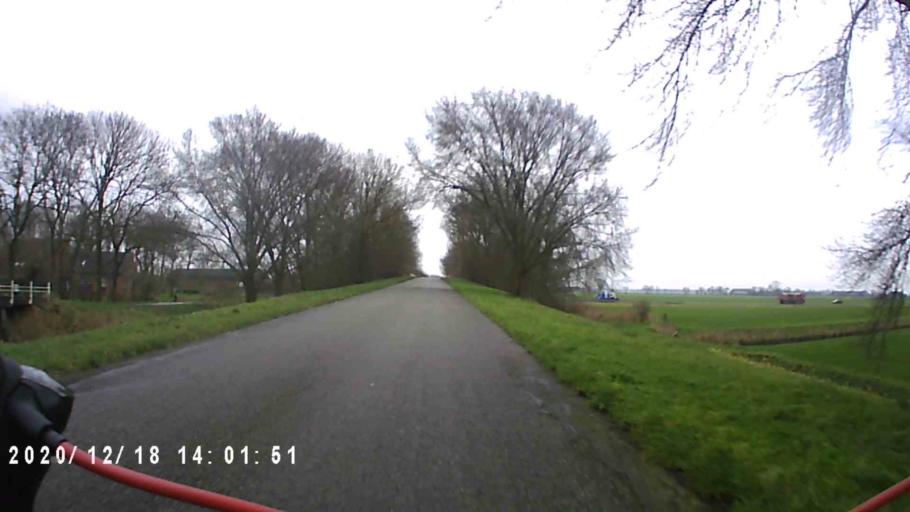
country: NL
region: Groningen
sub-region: Gemeente Bedum
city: Bedum
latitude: 53.2951
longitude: 6.6431
